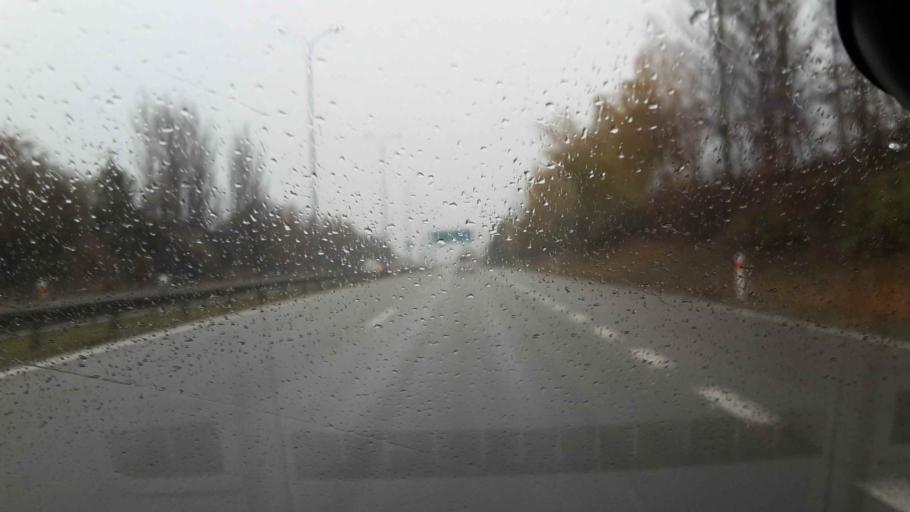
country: CZ
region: South Moravian
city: Podoli
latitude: 49.1844
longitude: 16.6843
